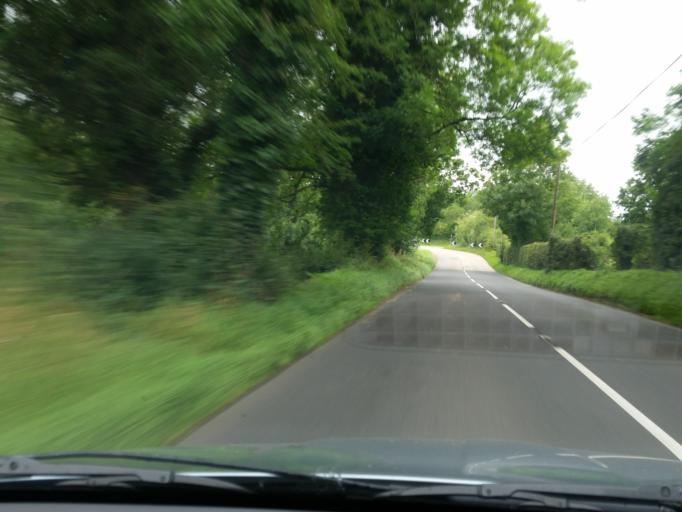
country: GB
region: Northern Ireland
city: Lisnaskea
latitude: 54.1964
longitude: -7.5276
